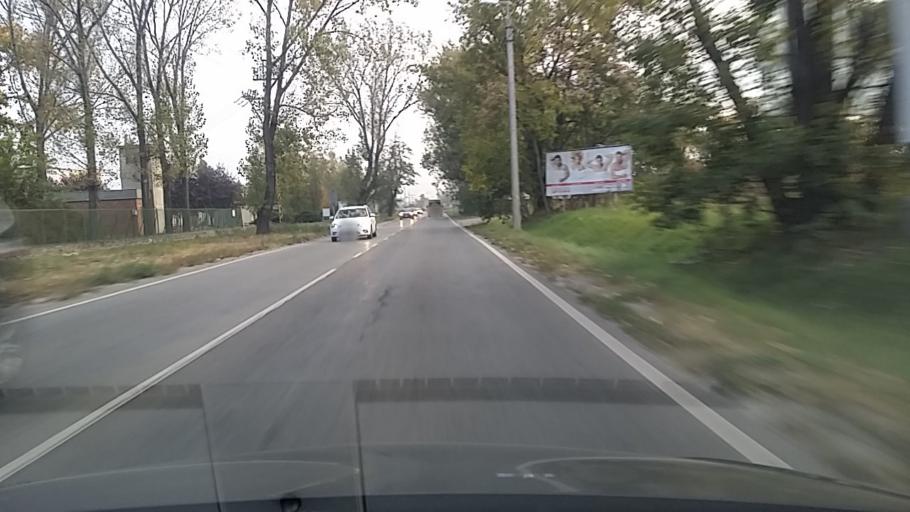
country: HU
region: Budapest
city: Budapest XV. keruelet
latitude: 47.5704
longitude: 19.1369
